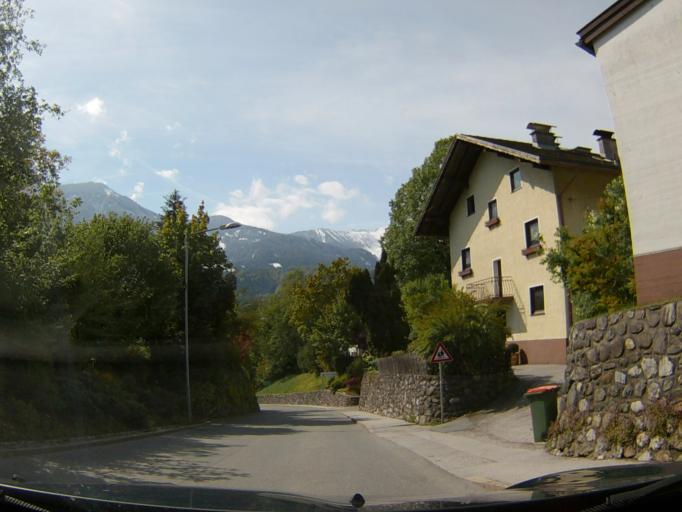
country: AT
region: Tyrol
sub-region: Politischer Bezirk Schwaz
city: Jenbach
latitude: 47.3938
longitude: 11.7715
